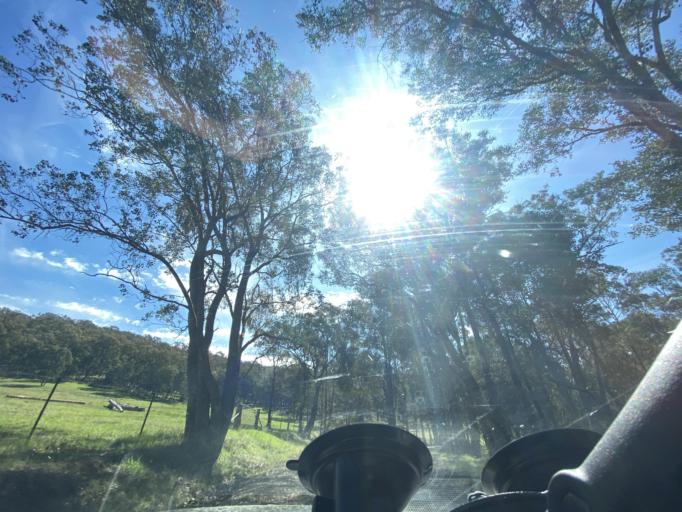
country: AU
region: Victoria
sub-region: Mansfield
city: Mansfield
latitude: -36.8056
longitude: 146.1230
